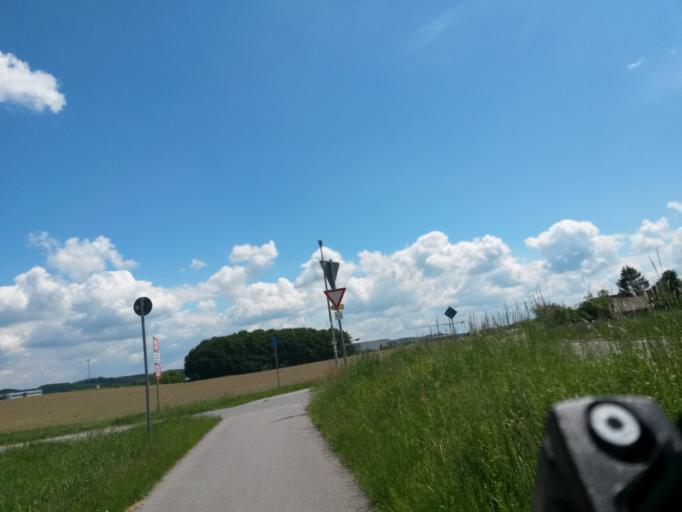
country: DE
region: Baden-Wuerttemberg
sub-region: Tuebingen Region
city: Bad Waldsee
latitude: 47.9399
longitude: 9.7487
